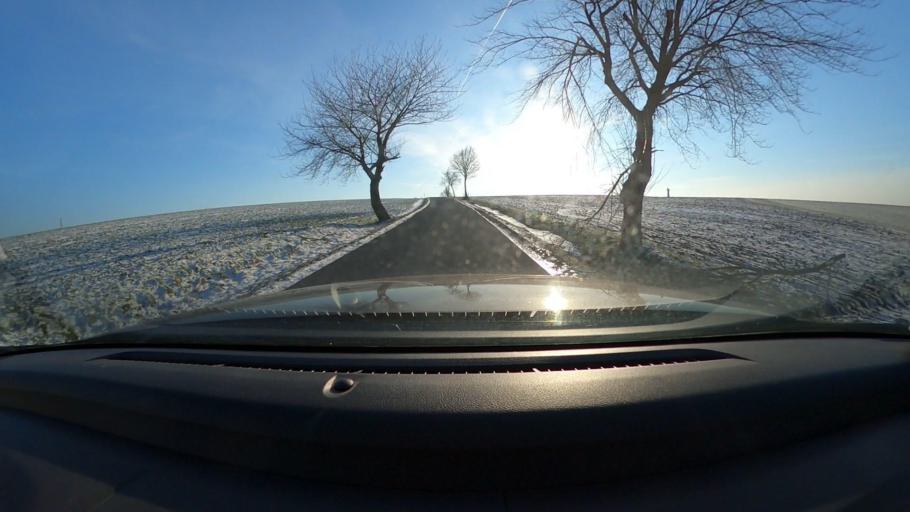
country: DE
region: Saxony
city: Frankenstein
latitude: 50.9489
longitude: 13.2263
